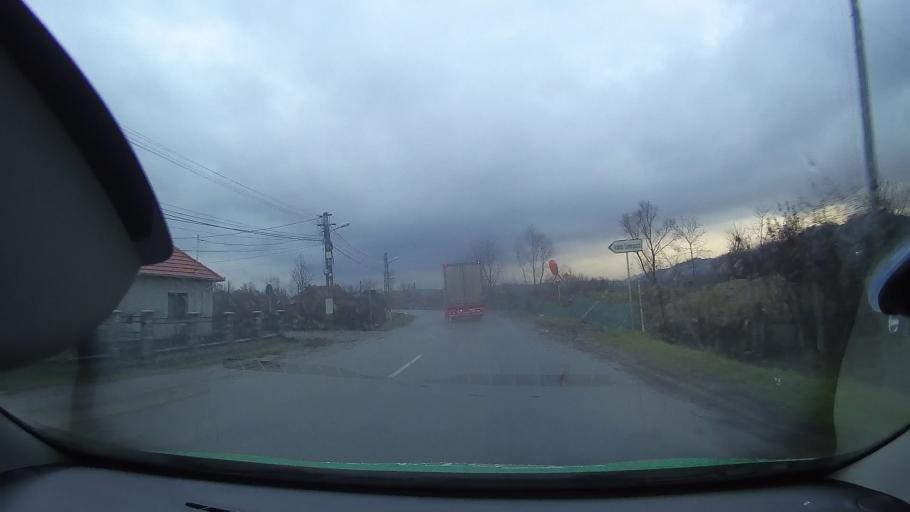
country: RO
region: Hunedoara
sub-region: Municipiul Brad
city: Brad
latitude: 46.1470
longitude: 22.7722
